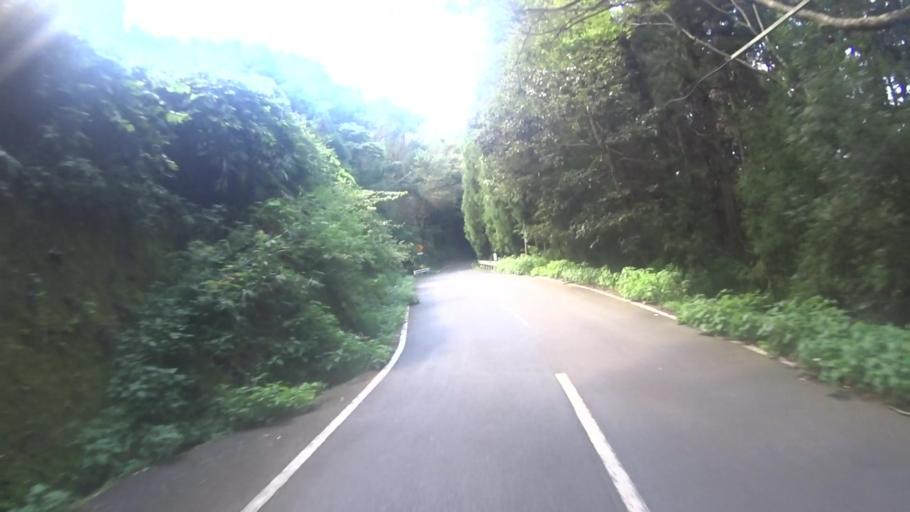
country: JP
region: Nara
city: Nara-shi
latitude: 34.7278
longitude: 135.8896
